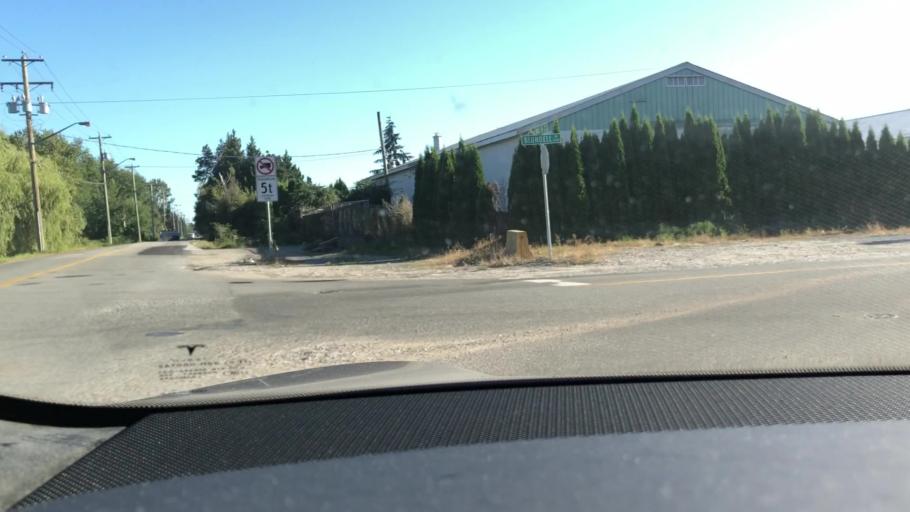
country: CA
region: British Columbia
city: Ladner
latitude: 49.1553
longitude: -123.0704
